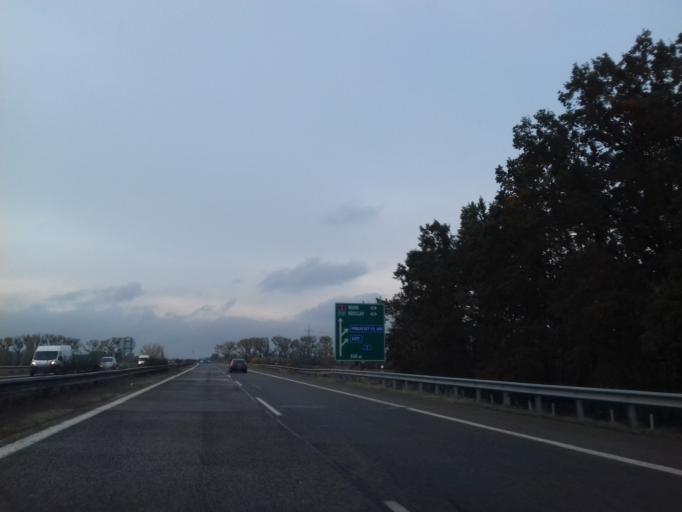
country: CZ
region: South Moravian
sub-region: Okres Breclav
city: Lanzhot
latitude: 48.6305
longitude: 17.0067
